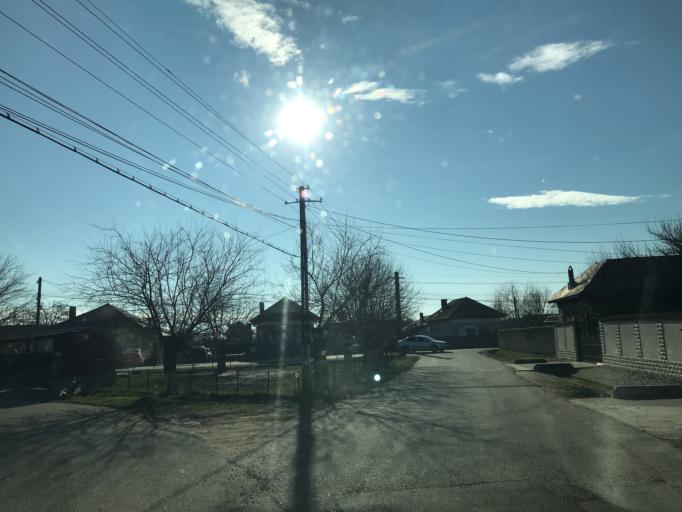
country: RO
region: Olt
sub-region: Comuna Slatioara
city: Slatioara
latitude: 44.3995
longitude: 24.3202
